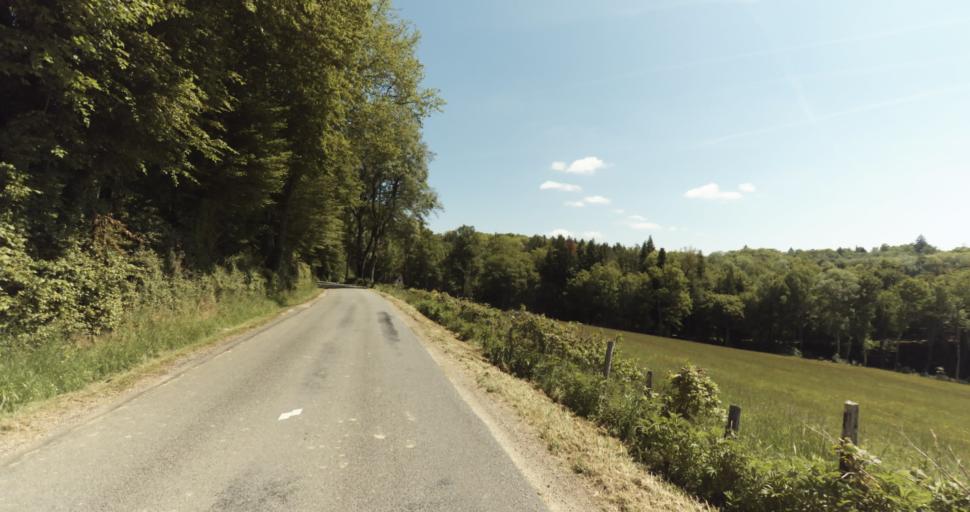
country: FR
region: Limousin
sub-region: Departement de la Haute-Vienne
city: Le Vigen
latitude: 45.7635
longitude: 1.2982
